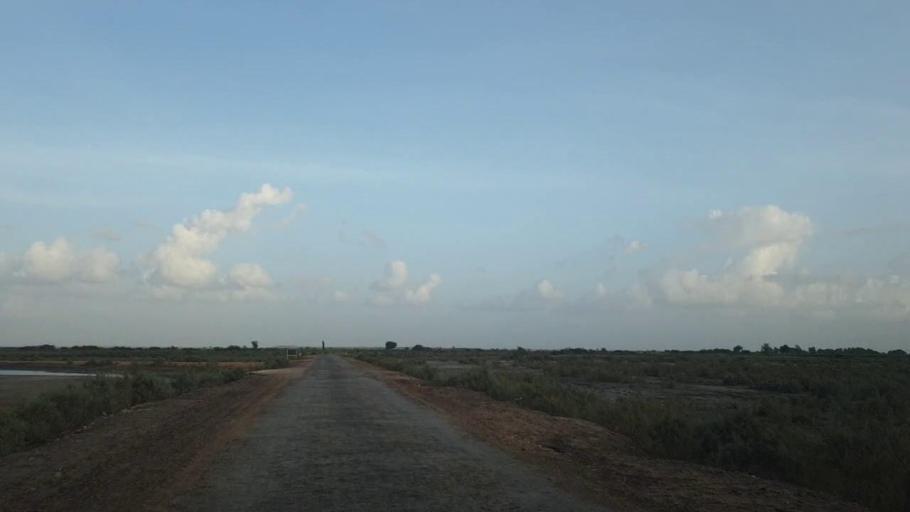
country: PK
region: Sindh
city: Kadhan
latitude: 24.5654
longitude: 69.1204
